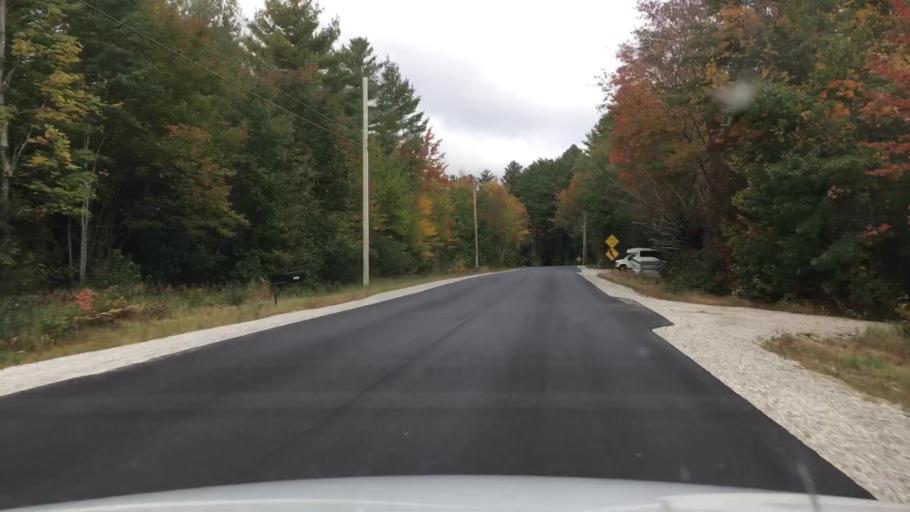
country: US
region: Maine
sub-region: Oxford County
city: Bethel
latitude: 44.3188
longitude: -70.7630
